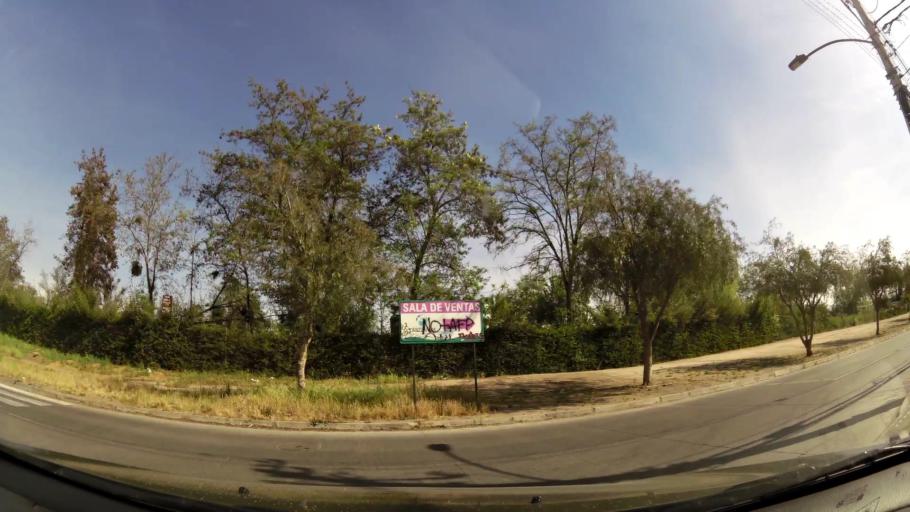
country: CL
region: Santiago Metropolitan
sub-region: Provincia de Cordillera
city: Puente Alto
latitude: -33.5939
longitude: -70.5503
